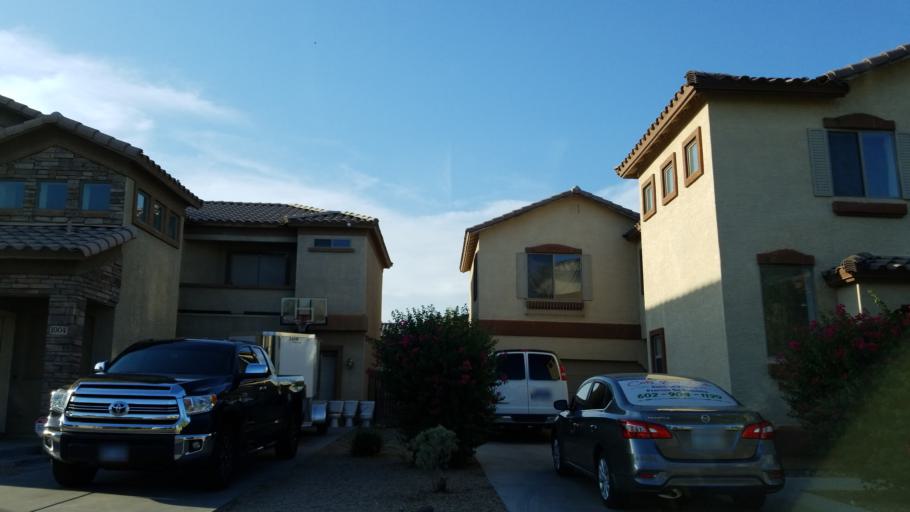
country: US
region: Arizona
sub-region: Maricopa County
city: Phoenix
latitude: 33.3928
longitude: -112.0852
